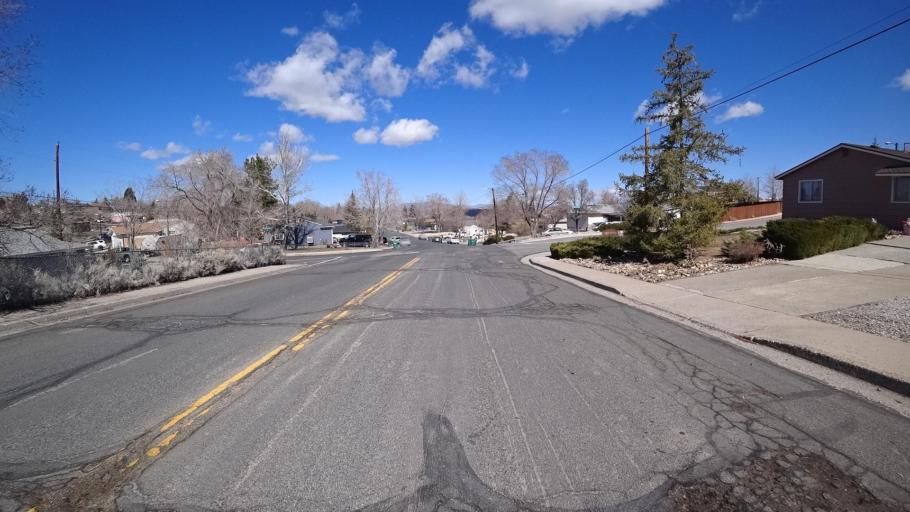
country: US
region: Nevada
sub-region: Washoe County
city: Golden Valley
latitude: 39.5899
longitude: -119.8414
